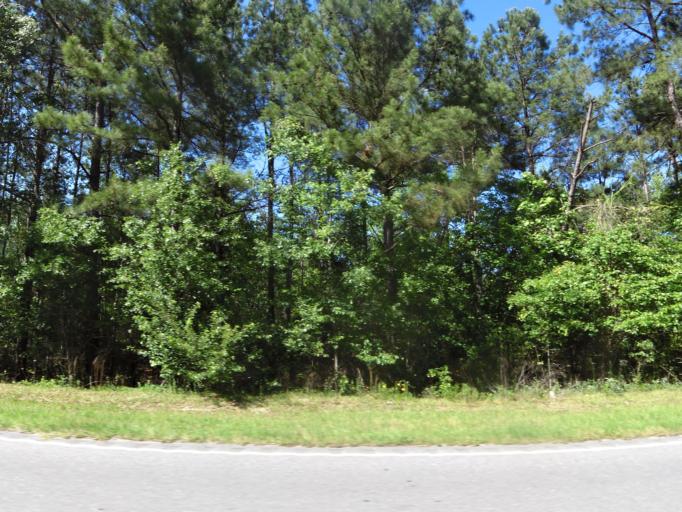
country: US
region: South Carolina
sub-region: Barnwell County
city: Williston
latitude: 33.3737
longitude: -81.3516
